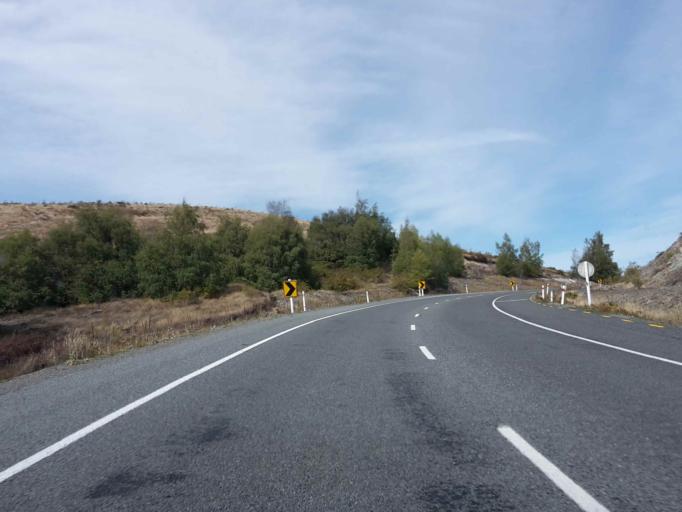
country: NZ
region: Canterbury
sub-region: Timaru District
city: Pleasant Point
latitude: -44.1688
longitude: 170.2139
